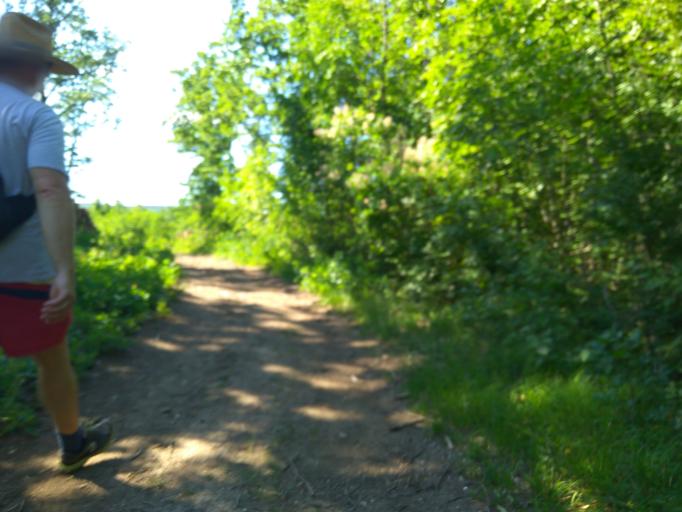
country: HU
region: Veszprem
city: Balatonfured
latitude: 46.9789
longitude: 17.8806
